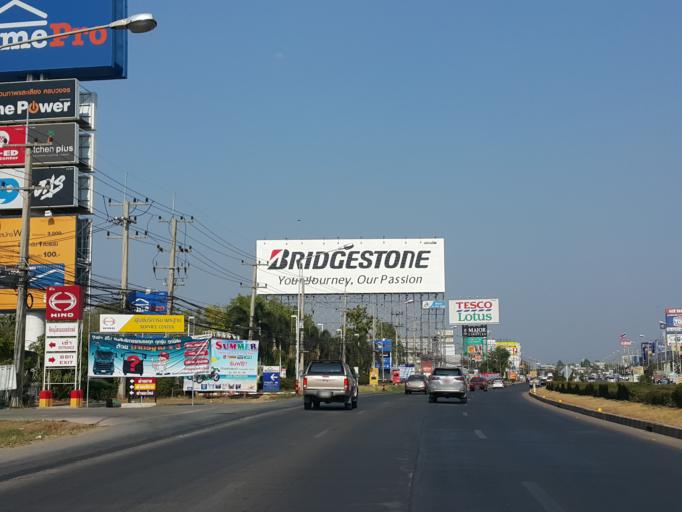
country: TH
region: Phitsanulok
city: Phitsanulok
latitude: 16.8179
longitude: 100.2970
